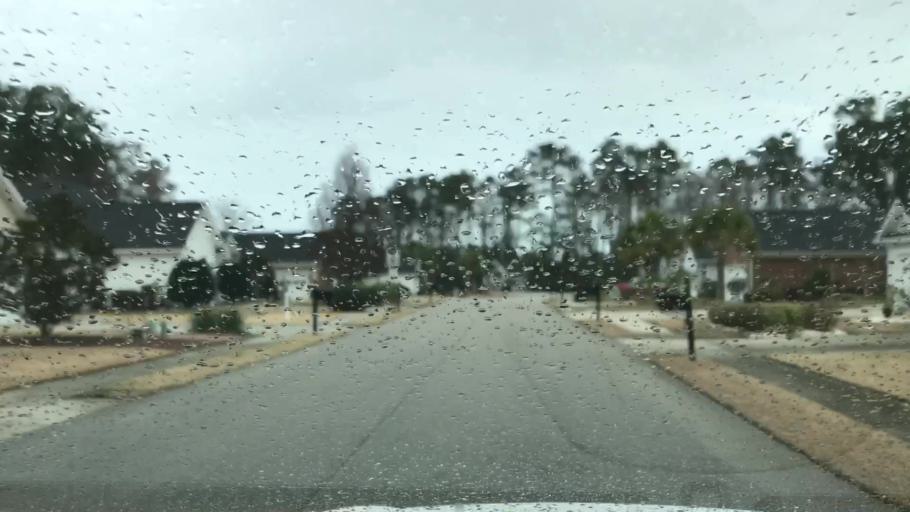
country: US
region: South Carolina
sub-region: Horry County
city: Red Hill
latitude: 33.7749
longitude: -79.0082
